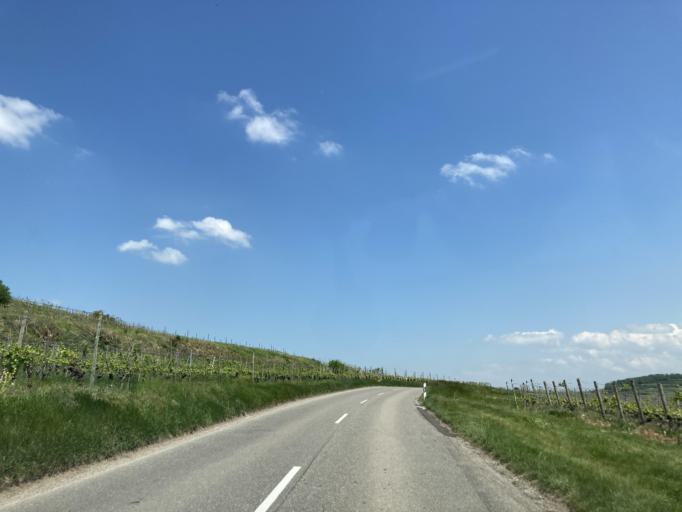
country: DE
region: Baden-Wuerttemberg
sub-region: Freiburg Region
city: Vogtsburg
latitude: 48.1050
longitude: 7.6102
